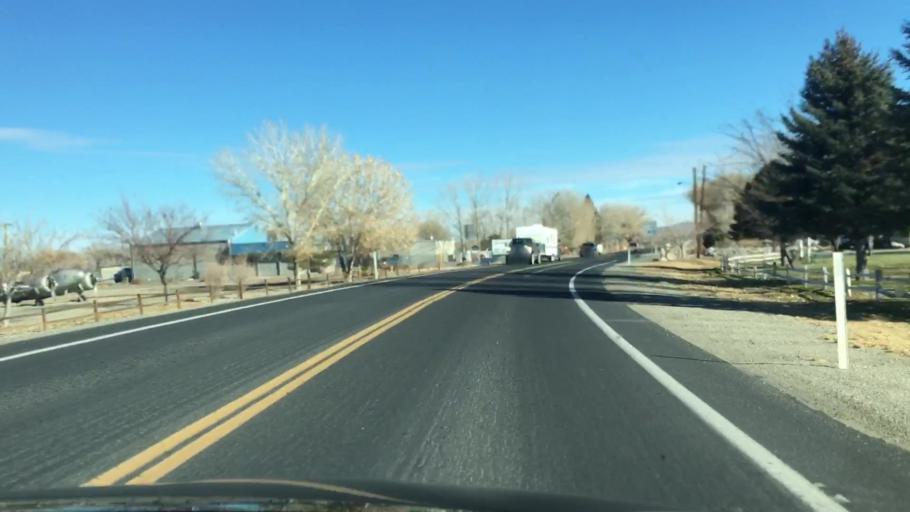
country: US
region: Nevada
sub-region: Lyon County
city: Yerington
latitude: 38.9974
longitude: -119.1595
